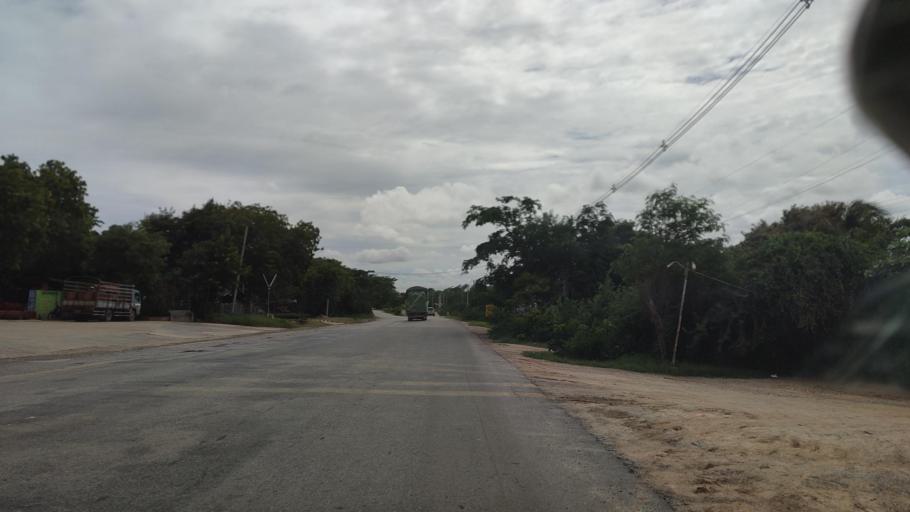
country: MM
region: Mandalay
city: Meiktila
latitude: 21.0853
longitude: 96.0115
